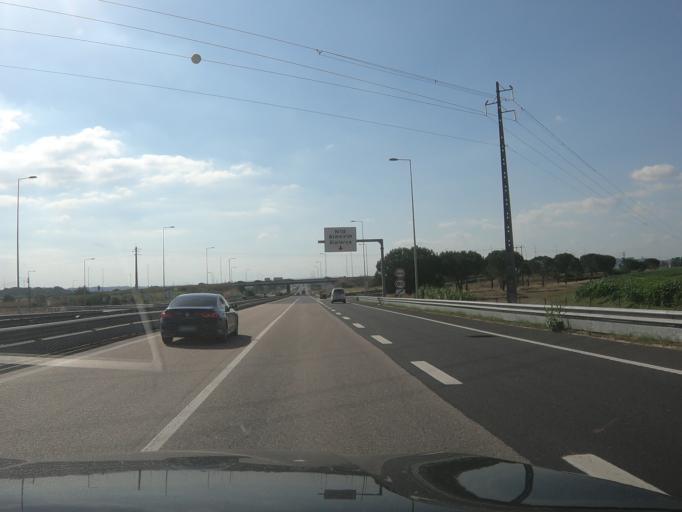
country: PT
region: Santarem
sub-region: Almeirim
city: Almeirim
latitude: 39.1888
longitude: -8.6457
